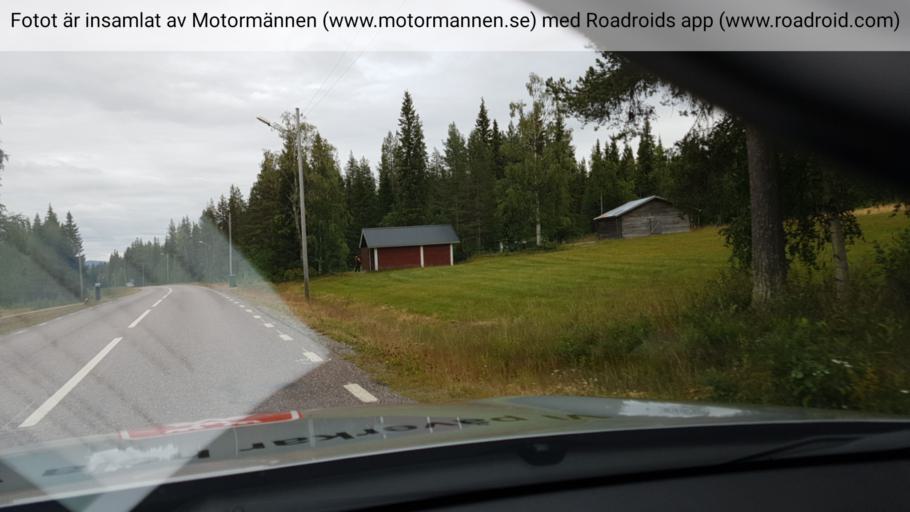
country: SE
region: Norrbotten
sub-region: Gallivare Kommun
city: Gaellivare
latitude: 67.0260
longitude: 21.7888
